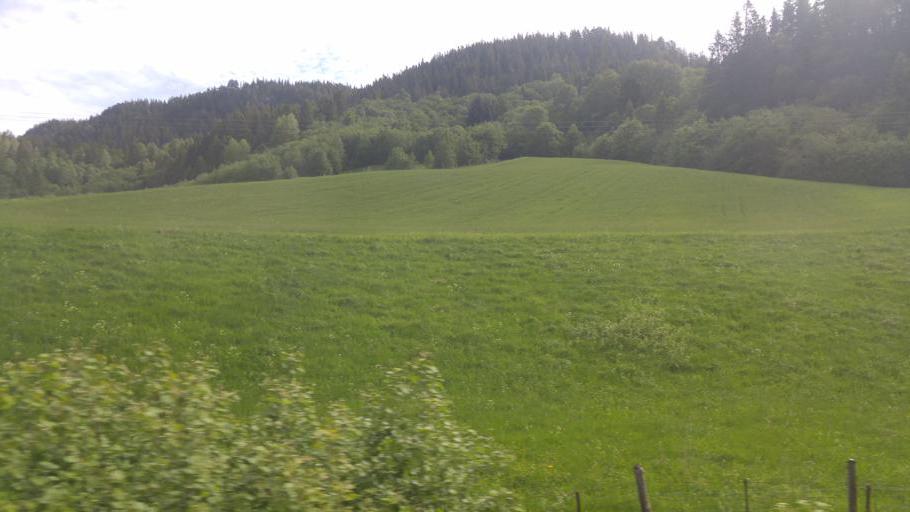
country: NO
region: Sor-Trondelag
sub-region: Melhus
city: Melhus
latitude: 63.2263
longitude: 10.2902
